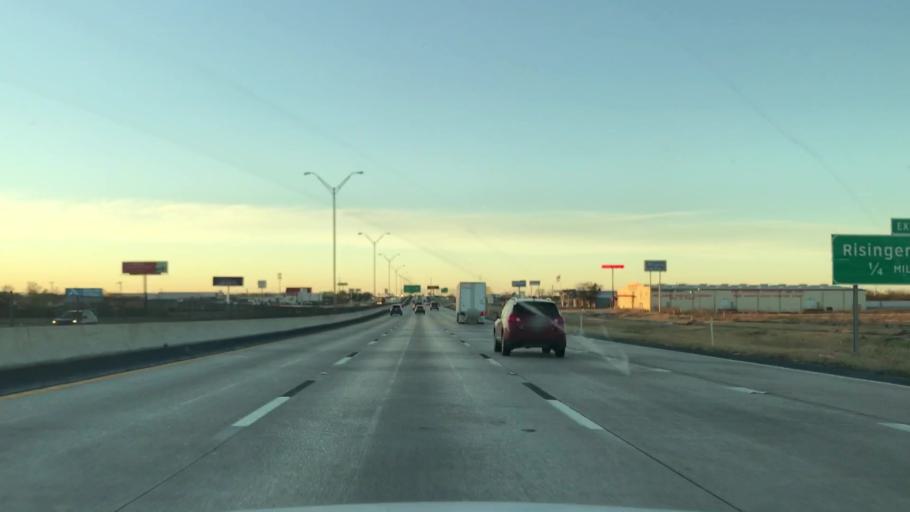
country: US
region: Texas
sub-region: Tarrant County
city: Everman
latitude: 32.6222
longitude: -97.3217
